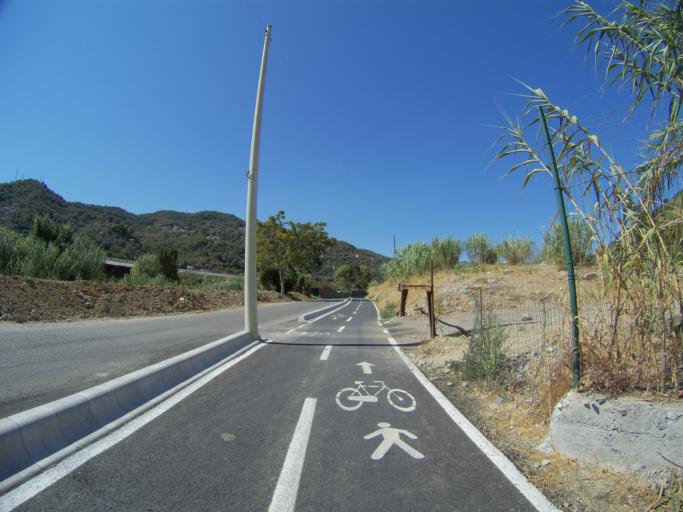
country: IT
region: Liguria
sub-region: Provincia di Imperia
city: Camporosso
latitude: 43.8197
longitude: 7.6321
